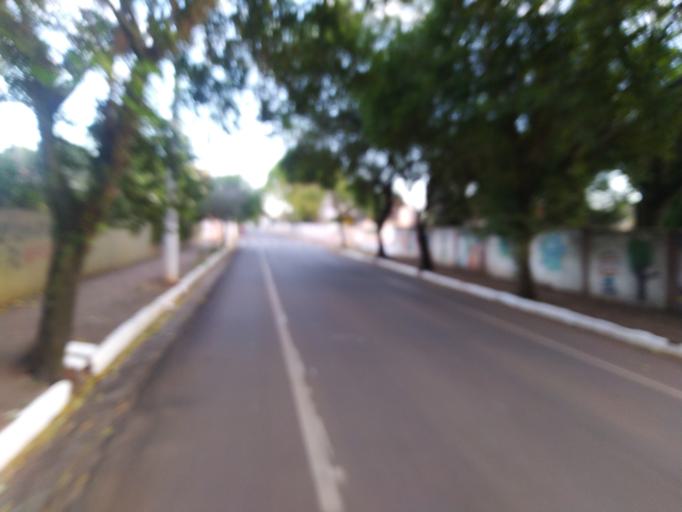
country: BR
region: Rio Grande do Sul
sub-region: Sao Borja
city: Sao Borja
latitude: -28.6530
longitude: -56.0066
